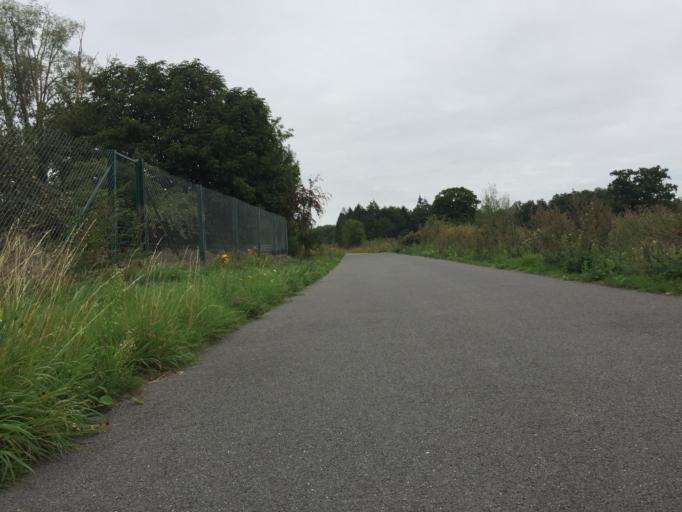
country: FR
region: Picardie
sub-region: Departement de l'Oise
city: Goincourt
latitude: 49.4132
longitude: 2.0252
